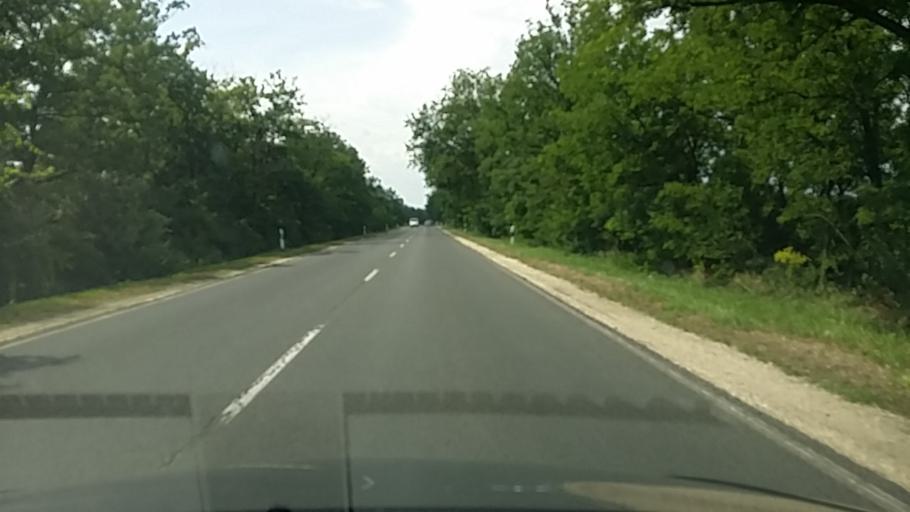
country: HU
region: Pest
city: Taborfalva
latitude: 47.1015
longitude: 19.4681
